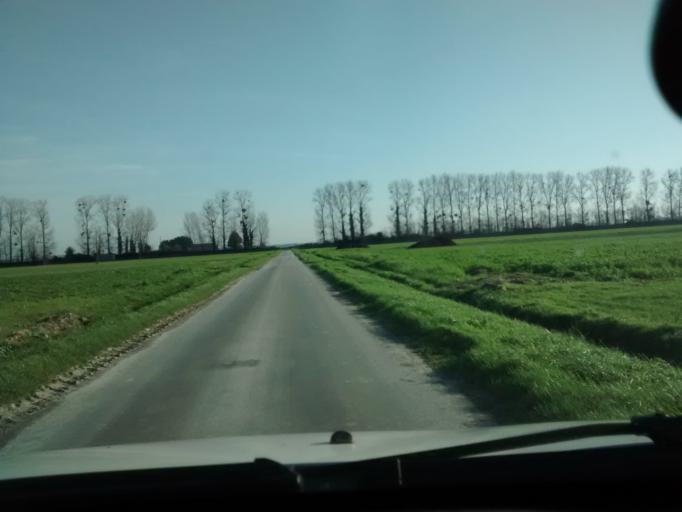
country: FR
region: Brittany
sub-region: Departement d'Ille-et-Vilaine
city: Roz-sur-Couesnon
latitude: 48.5931
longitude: -1.5510
